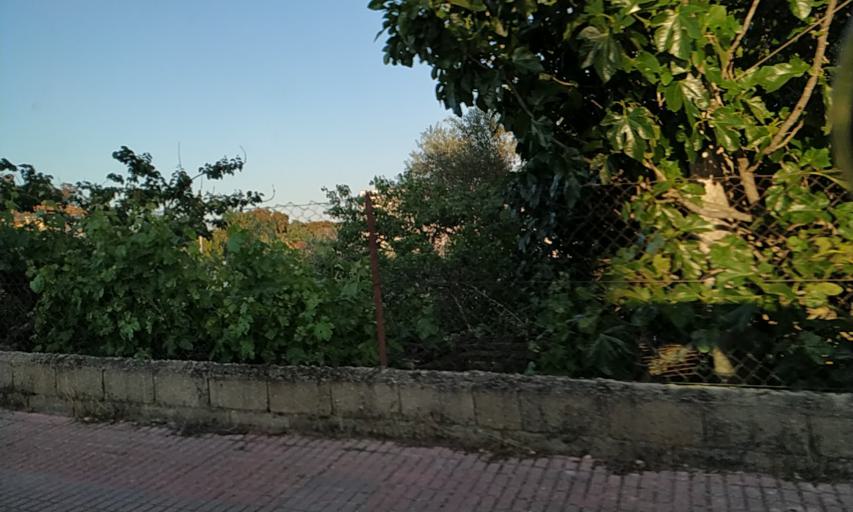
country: ES
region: Extremadura
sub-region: Provincia de Caceres
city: Valencia de Alcantara
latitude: 39.4049
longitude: -7.2495
